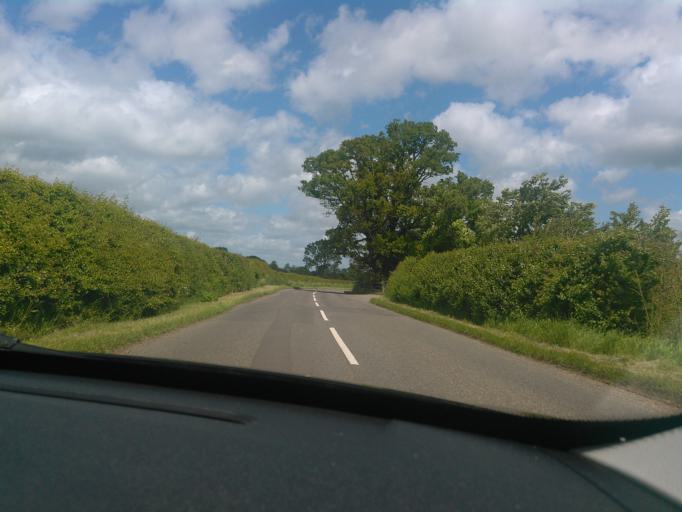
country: GB
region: England
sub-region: Shropshire
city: Prees
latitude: 52.8700
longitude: -2.6640
